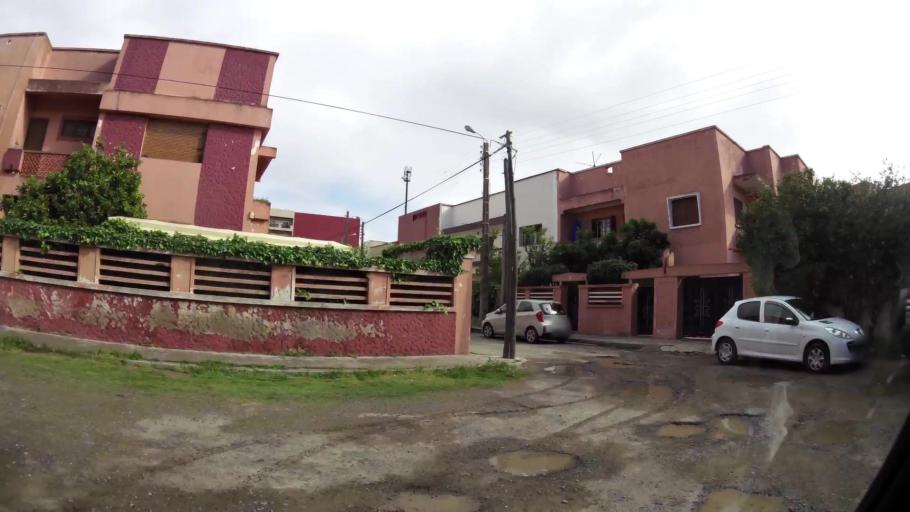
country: MA
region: Doukkala-Abda
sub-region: El-Jadida
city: El Jadida
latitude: 33.2442
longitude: -8.4976
